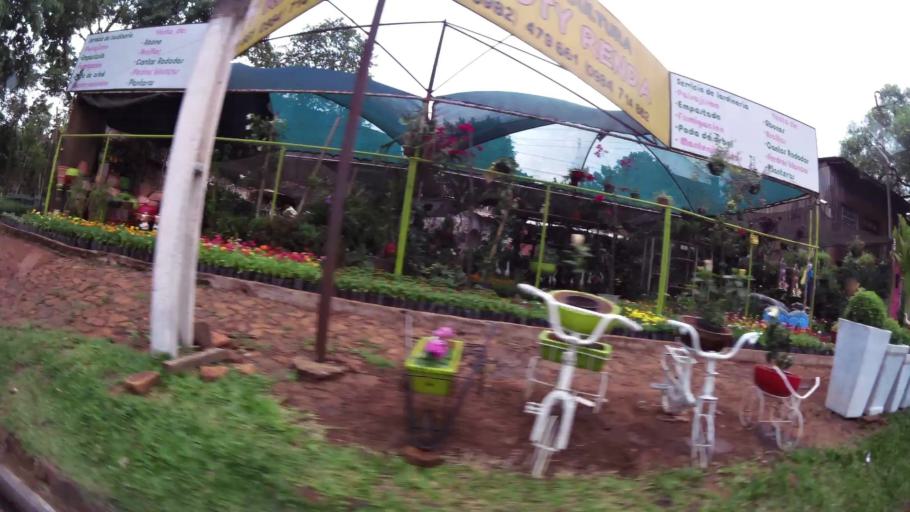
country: PY
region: Alto Parana
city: Presidente Franco
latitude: -25.5449
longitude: -54.6090
